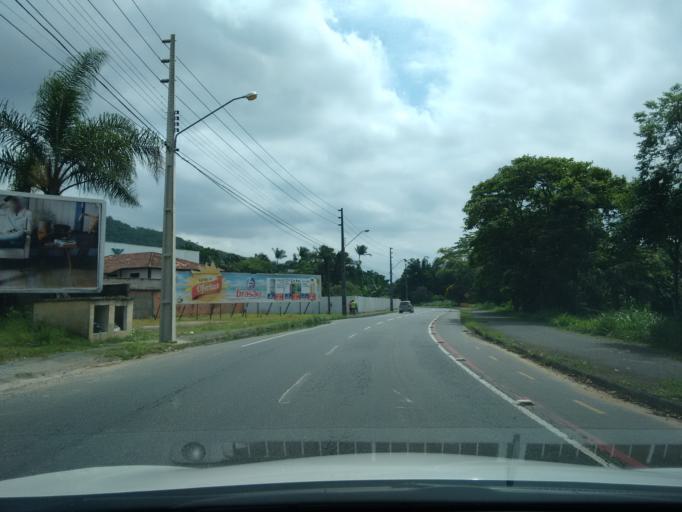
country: BR
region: Santa Catarina
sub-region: Jaragua Do Sul
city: Jaragua do Sul
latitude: -26.4914
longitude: -49.0679
